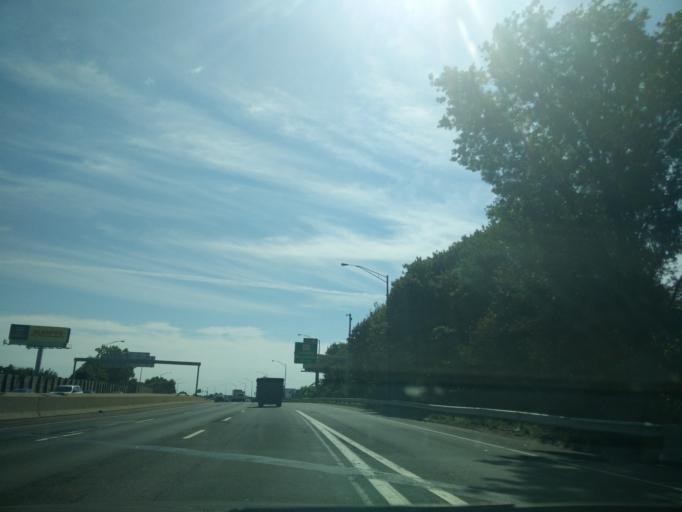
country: US
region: Connecticut
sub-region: Fairfield County
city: Bridgeport
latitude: 41.1758
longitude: -73.1699
